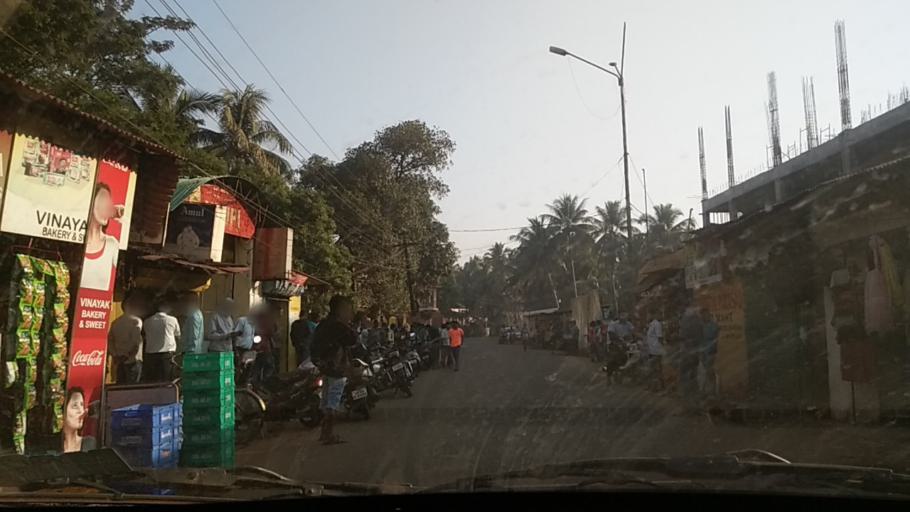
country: IN
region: Goa
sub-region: South Goa
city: Cuncolim
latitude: 15.1792
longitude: 73.9988
